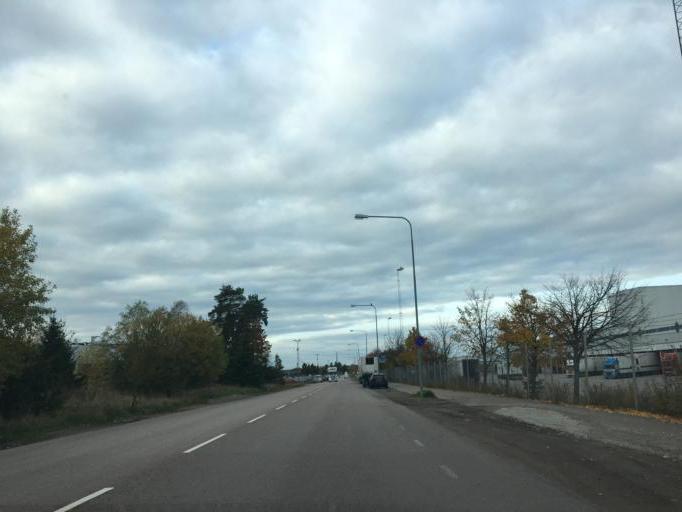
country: SE
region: Vaestmanland
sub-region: Vasteras
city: Vasteras
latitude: 59.5863
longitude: 16.4779
